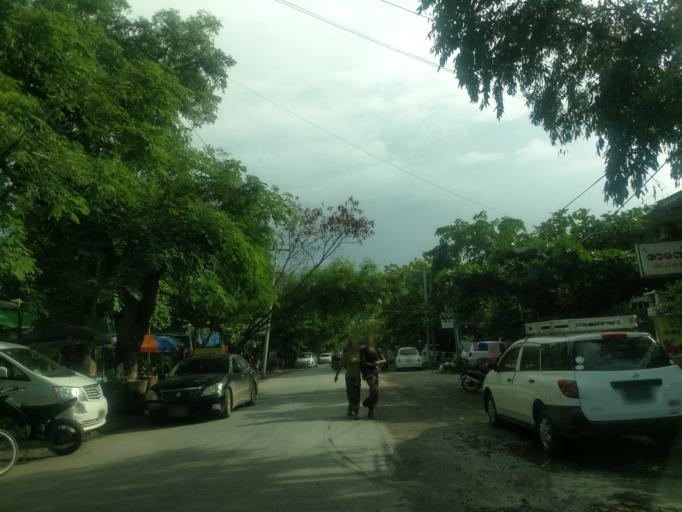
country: MM
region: Mandalay
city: Mandalay
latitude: 21.9777
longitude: 96.1005
